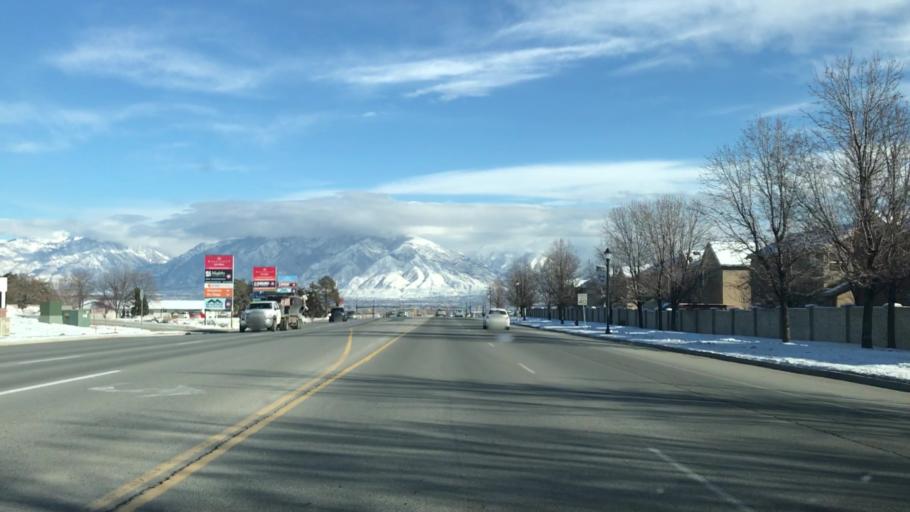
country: US
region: Utah
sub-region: Salt Lake County
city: Herriman
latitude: 40.5078
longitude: -112.0097
